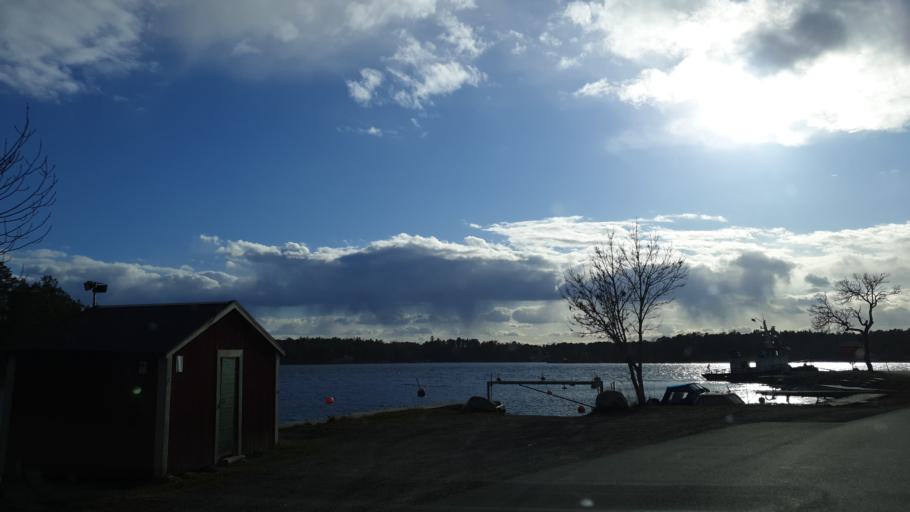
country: SE
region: Stockholm
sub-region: Varmdo Kommun
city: Holo
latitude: 59.3607
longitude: 18.6488
